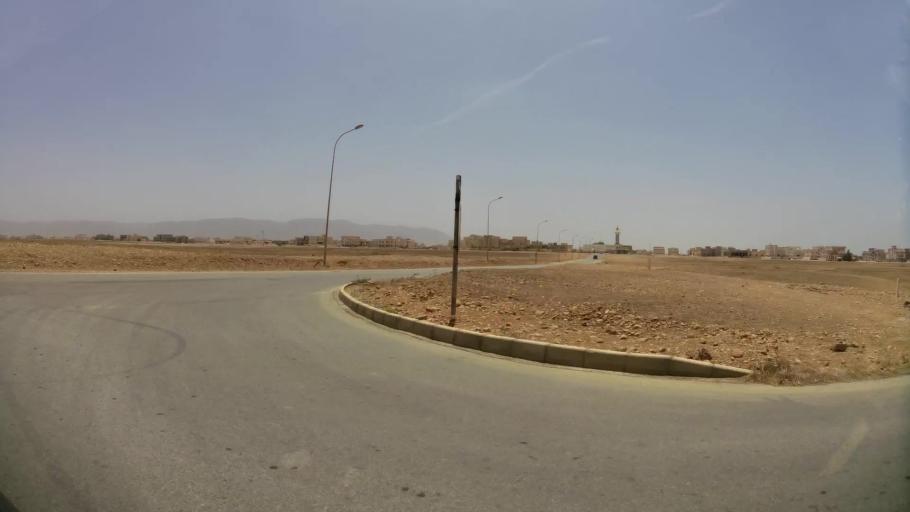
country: OM
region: Zufar
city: Salalah
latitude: 17.0563
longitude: 54.2075
